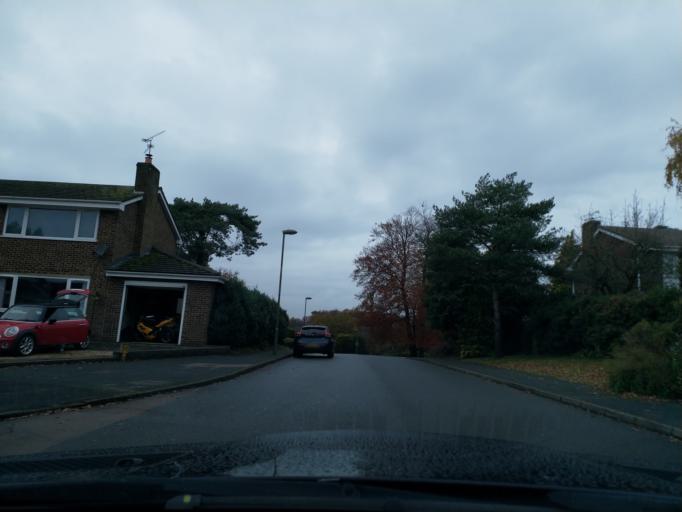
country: GB
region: England
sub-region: Surrey
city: Frimley
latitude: 51.3184
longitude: -0.7267
